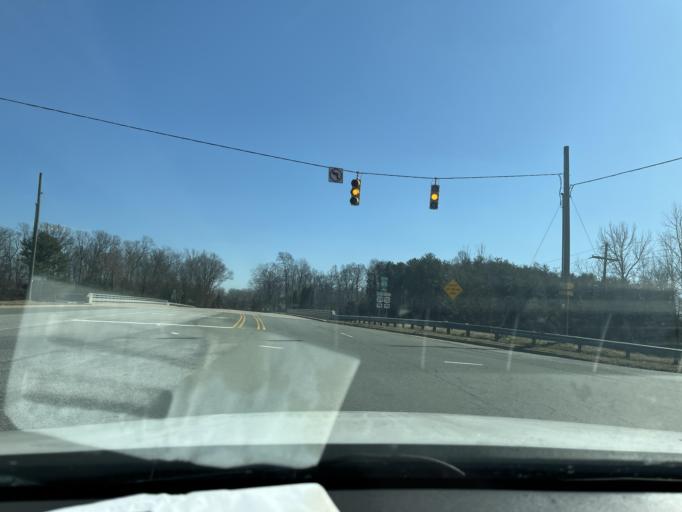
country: US
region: North Carolina
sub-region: Guilford County
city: Jamestown
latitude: 35.9820
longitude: -79.9024
